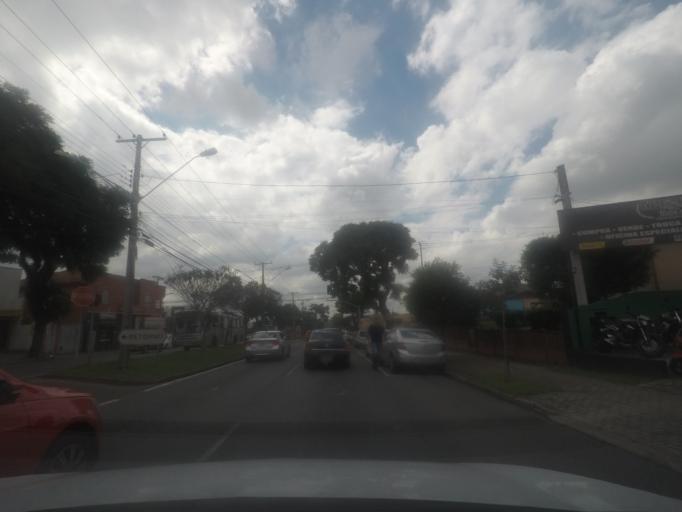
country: BR
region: Parana
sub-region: Curitiba
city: Curitiba
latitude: -25.4545
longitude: -49.2664
